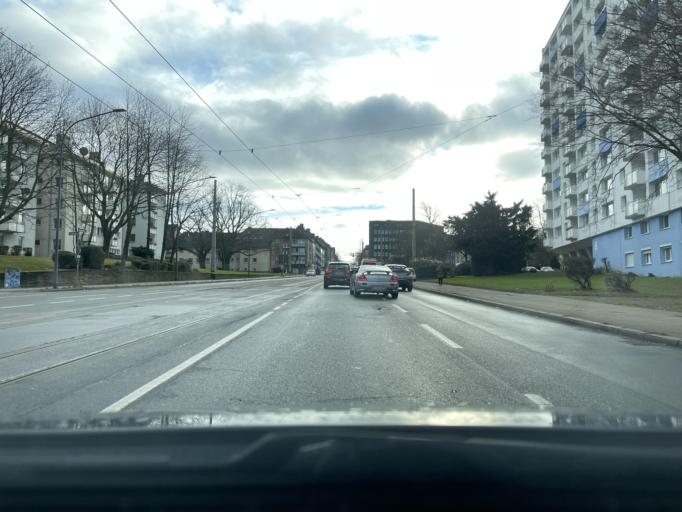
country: DE
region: North Rhine-Westphalia
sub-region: Regierungsbezirk Dusseldorf
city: Essen
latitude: 51.4441
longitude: 6.9867
